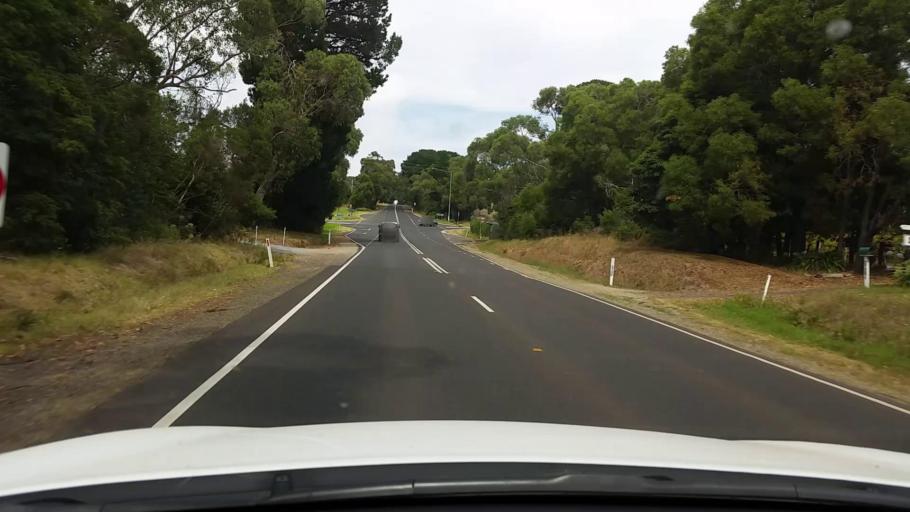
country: AU
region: Victoria
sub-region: Mornington Peninsula
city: Merricks
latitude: -38.4057
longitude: 145.0667
